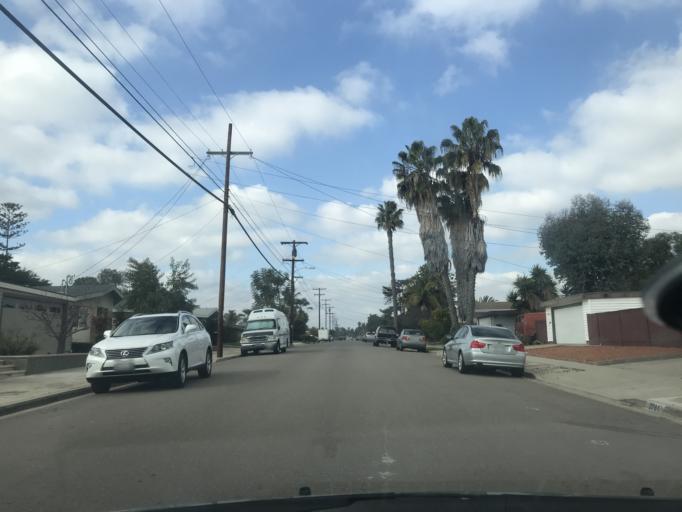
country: US
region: California
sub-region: San Diego County
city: San Diego
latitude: 32.7958
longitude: -117.1239
